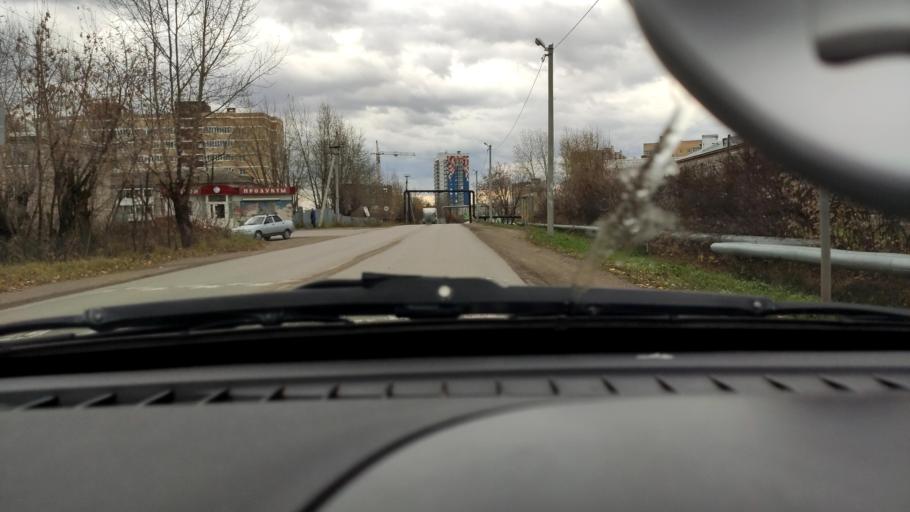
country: RU
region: Perm
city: Kondratovo
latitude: 57.9815
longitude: 56.1057
